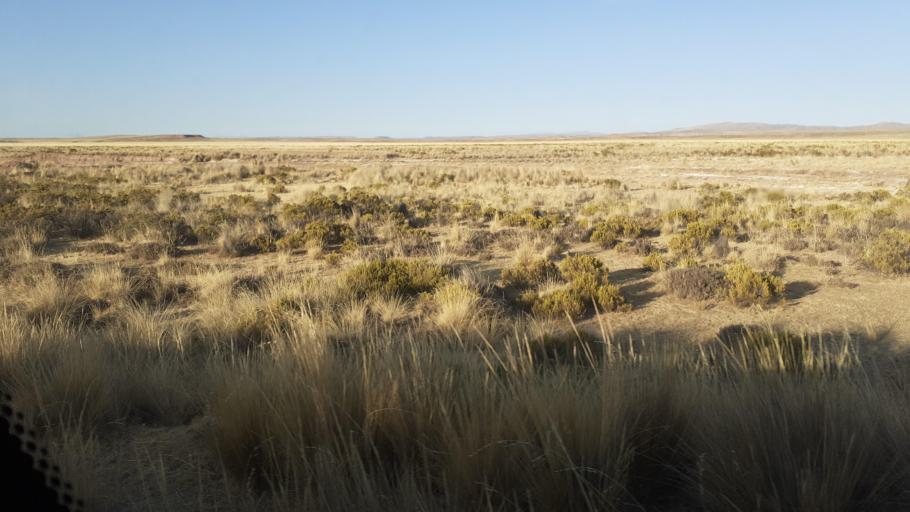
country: BO
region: La Paz
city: Tiahuanaco
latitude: -16.9415
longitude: -68.7637
